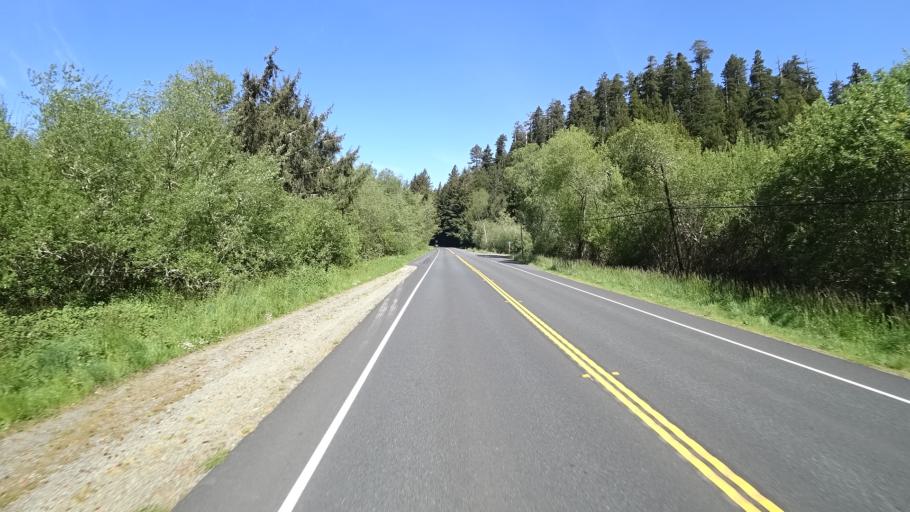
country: US
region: California
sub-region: Del Norte County
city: Bertsch-Oceanview
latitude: 41.5611
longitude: -124.0622
